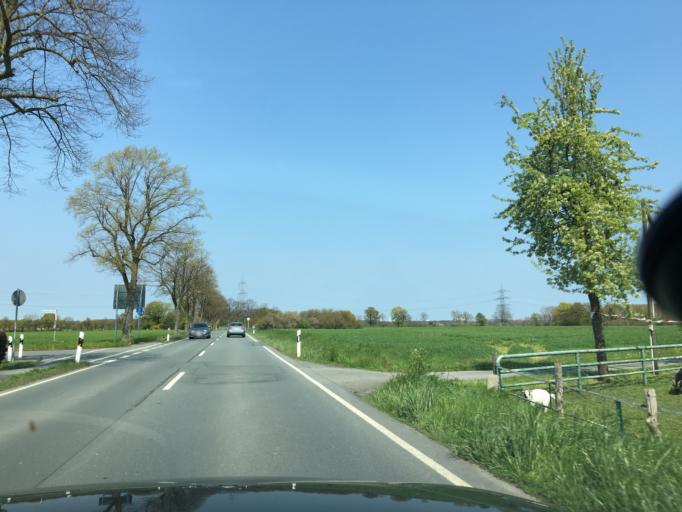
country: DE
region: North Rhine-Westphalia
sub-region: Regierungsbezirk Munster
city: Muenster
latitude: 51.8974
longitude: 7.5810
